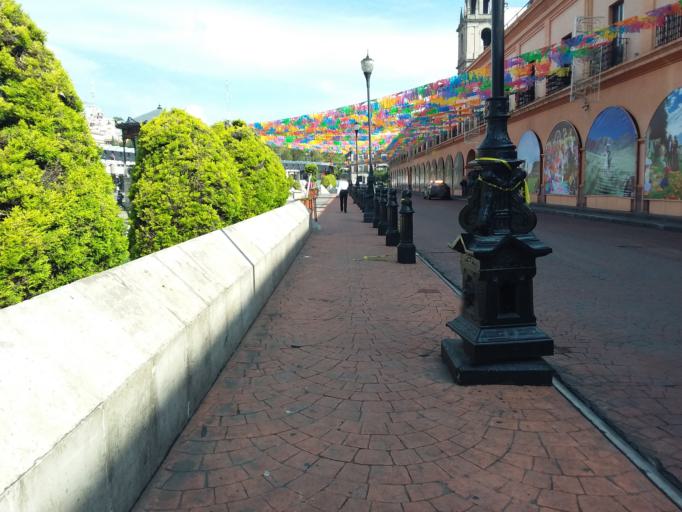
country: MX
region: Mexico
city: Toluca
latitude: 19.2907
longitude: -99.6578
